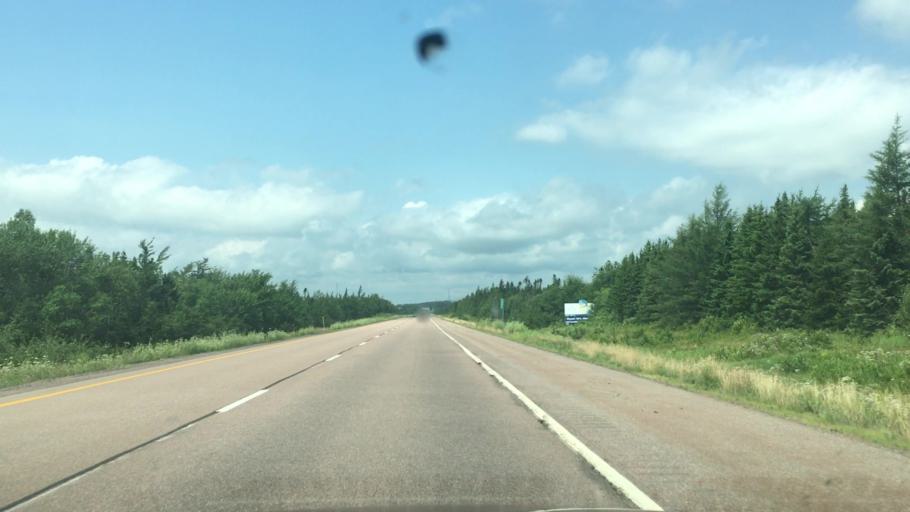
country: CA
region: New Brunswick
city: Sackville
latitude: 45.9805
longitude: -64.4604
